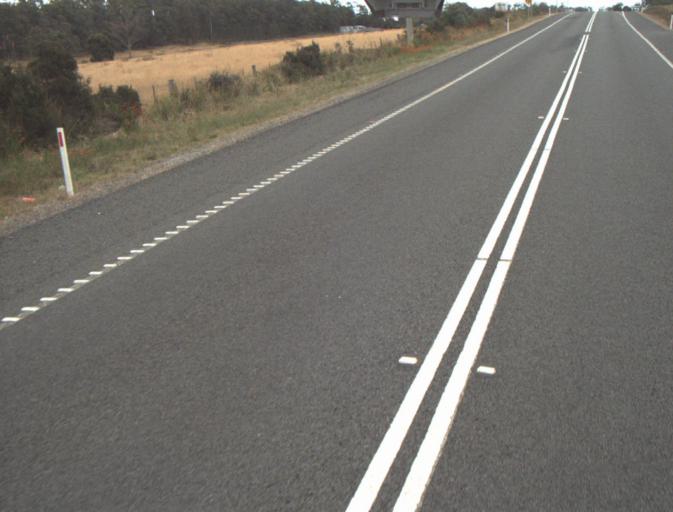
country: AU
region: Tasmania
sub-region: Launceston
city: Mayfield
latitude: -41.2523
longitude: 147.0227
